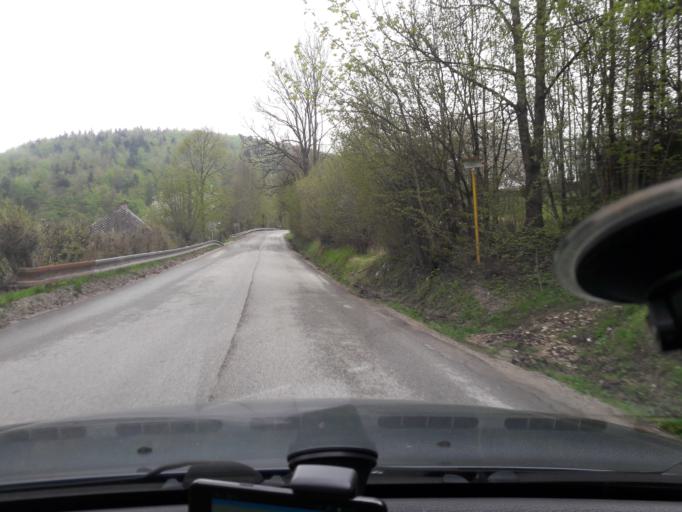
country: SK
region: Banskobystricky
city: Revuca
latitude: 48.7783
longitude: 20.1101
